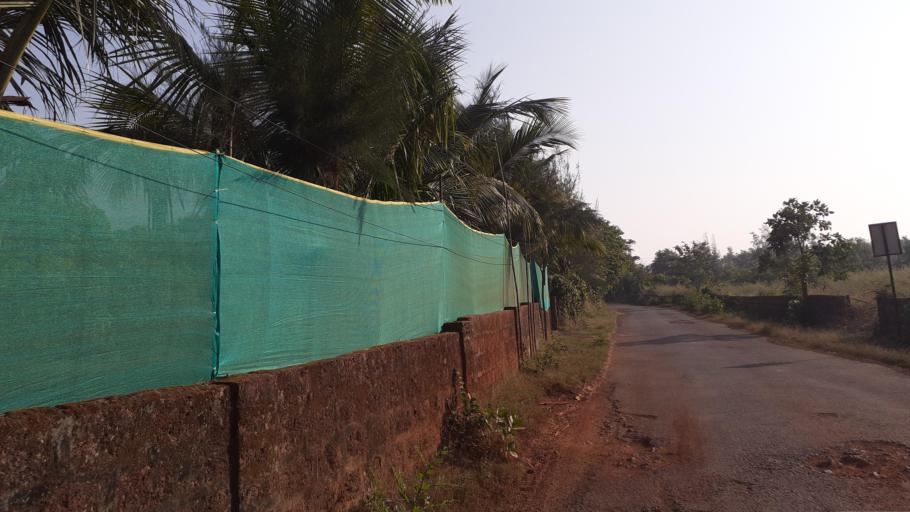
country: IN
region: Maharashtra
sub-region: Ratnagiri
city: Ratnagiri
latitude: 17.2122
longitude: 73.2490
